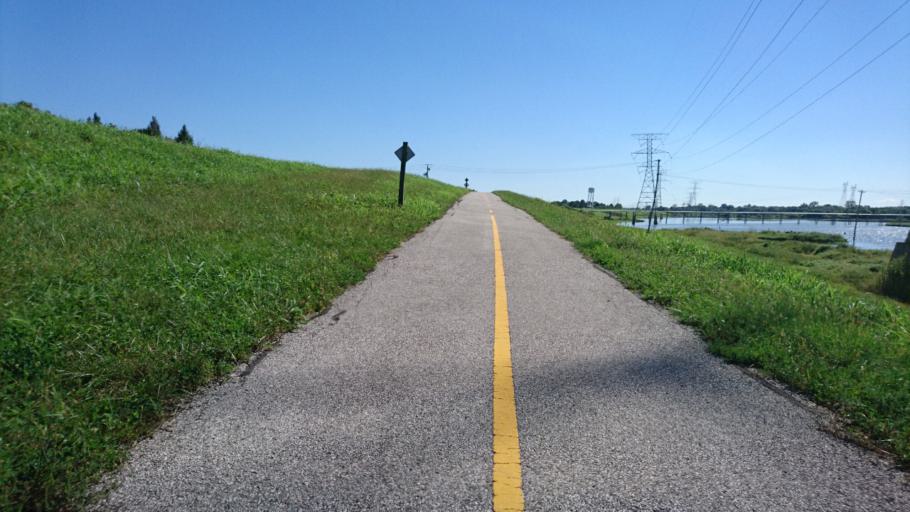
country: US
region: Illinois
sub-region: Madison County
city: Hartford
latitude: 38.8407
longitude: -90.0983
